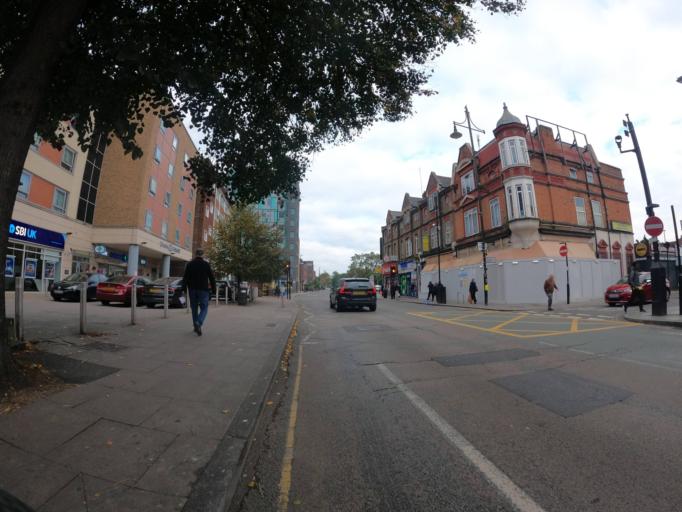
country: GB
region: England
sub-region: Greater London
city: Southall
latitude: 51.5111
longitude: -0.3742
